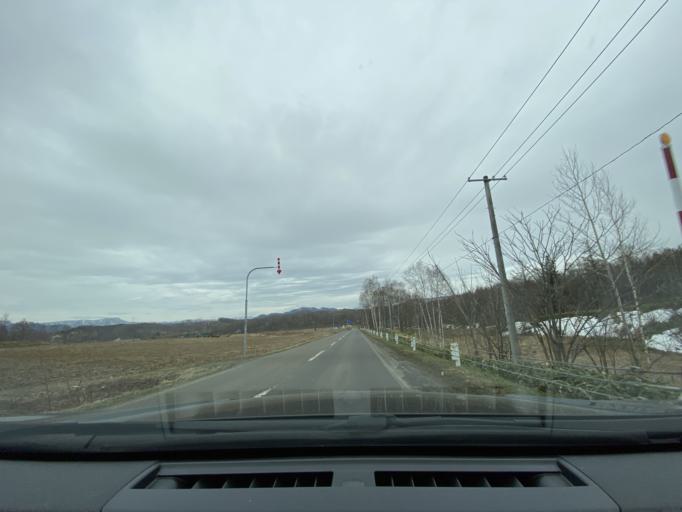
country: JP
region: Hokkaido
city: Nayoro
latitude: 44.0928
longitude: 142.4679
